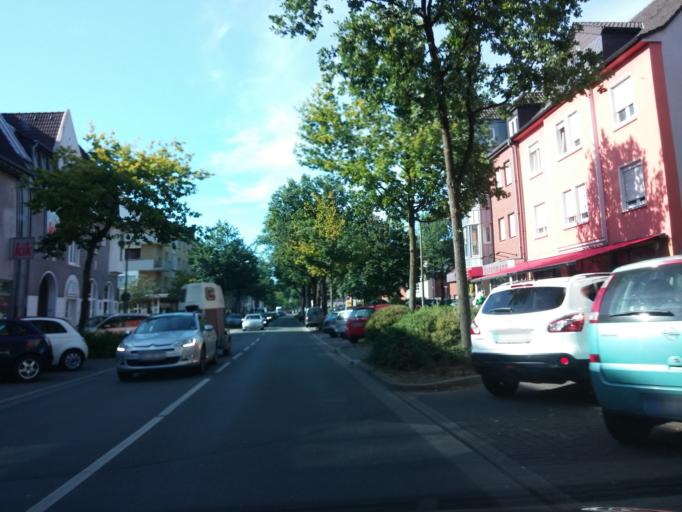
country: DE
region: North Rhine-Westphalia
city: Dorsten
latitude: 51.6800
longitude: 6.9580
